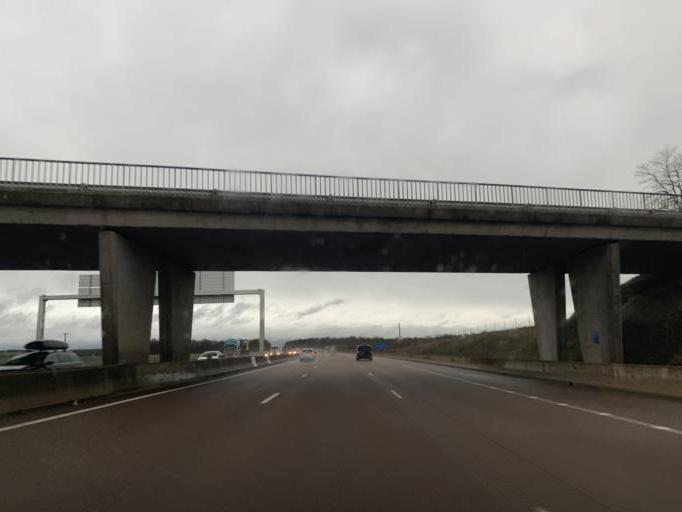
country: FR
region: Champagne-Ardenne
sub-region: Departement de la Haute-Marne
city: Langres
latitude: 47.7945
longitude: 5.2245
